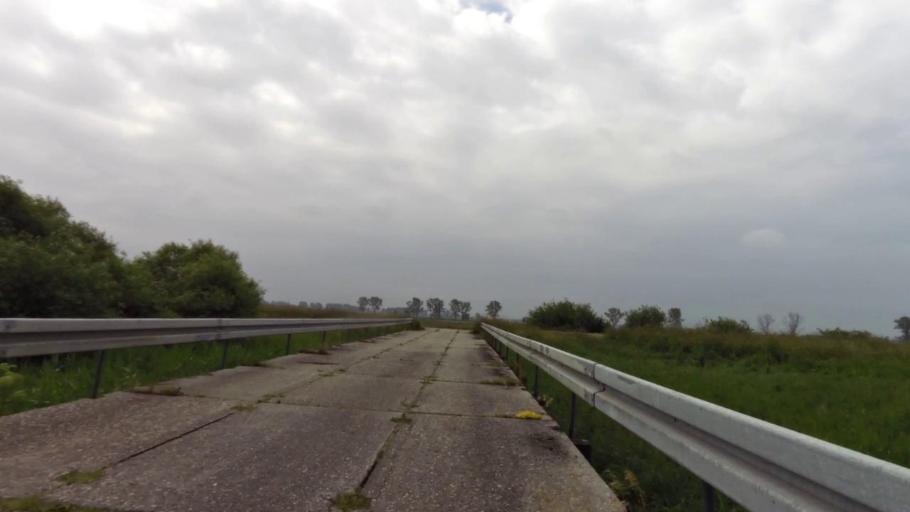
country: PL
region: West Pomeranian Voivodeship
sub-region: Powiat goleniowski
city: Stepnica
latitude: 53.5533
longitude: 14.7031
